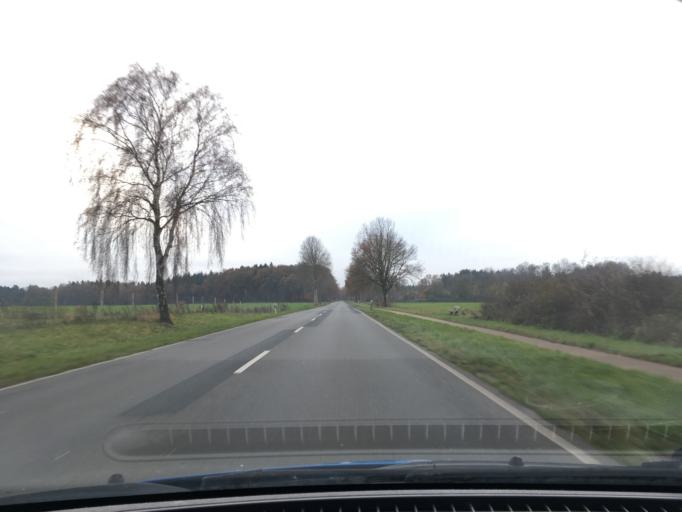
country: DE
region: Lower Saxony
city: Embsen
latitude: 53.2071
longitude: 10.3646
